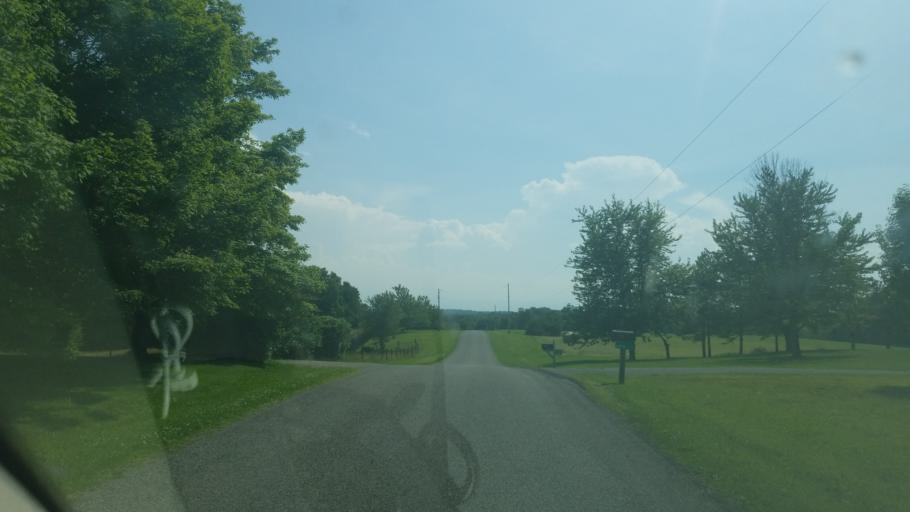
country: US
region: Ohio
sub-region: Champaign County
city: North Lewisburg
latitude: 40.2840
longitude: -83.6364
